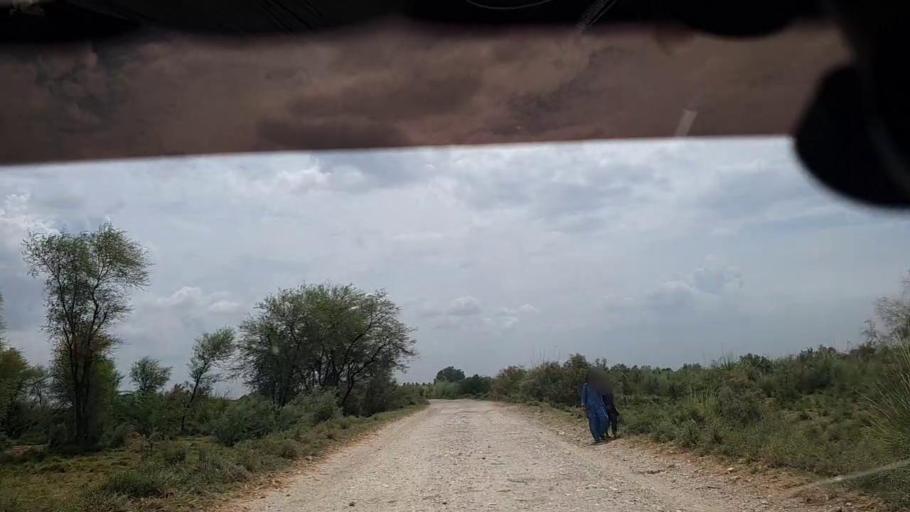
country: PK
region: Sindh
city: Rustam jo Goth
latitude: 28.0598
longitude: 68.9402
